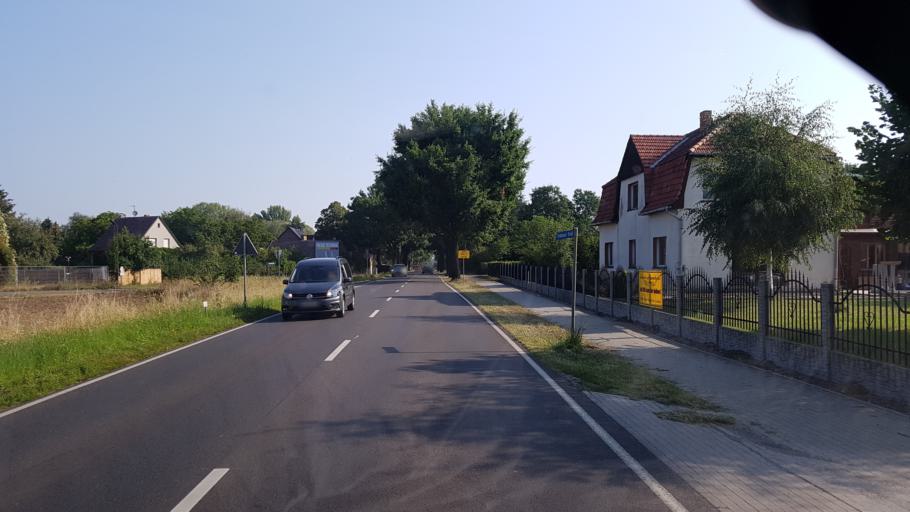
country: DE
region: Brandenburg
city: Kolkwitz
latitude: 51.7100
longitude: 14.2850
